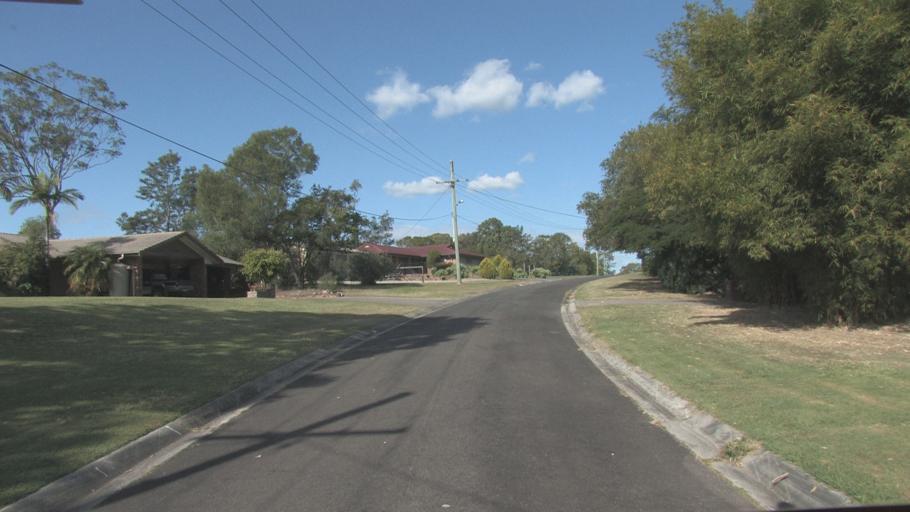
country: AU
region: Queensland
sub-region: Logan
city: Windaroo
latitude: -27.7341
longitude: 153.1892
